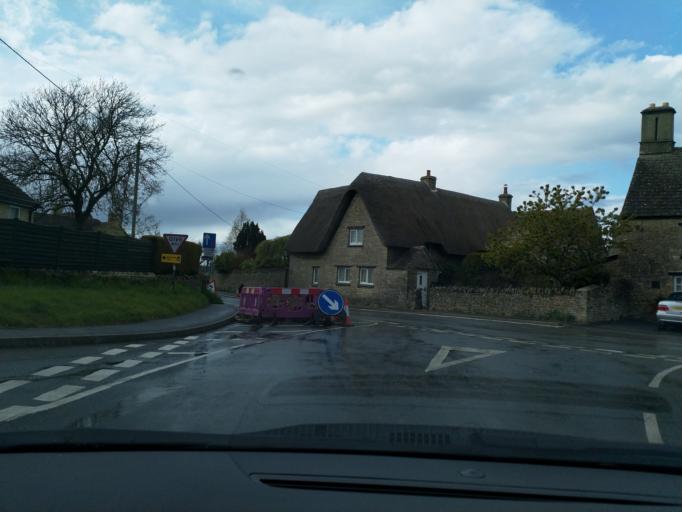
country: GB
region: England
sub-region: Oxfordshire
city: North Leigh
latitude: 51.8143
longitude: -1.4414
